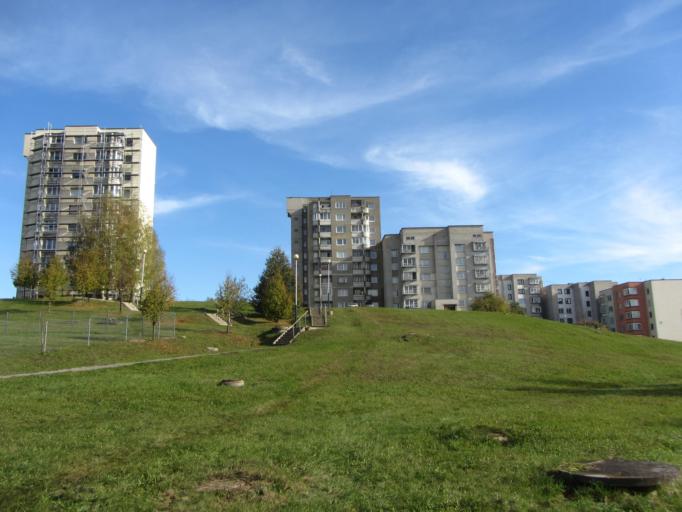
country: LT
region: Vilnius County
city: Elektrenai
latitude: 54.7854
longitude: 24.6821
